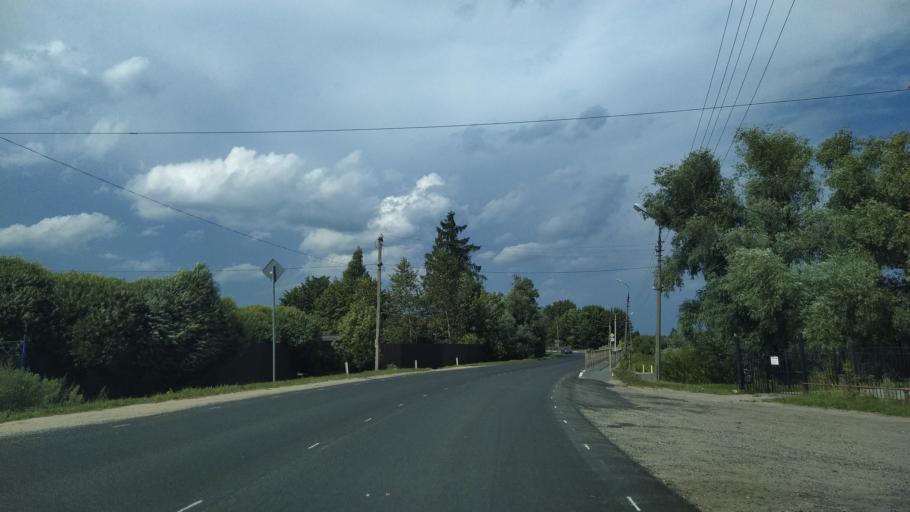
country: RU
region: Pskov
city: Porkhov
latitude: 57.7678
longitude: 29.5527
